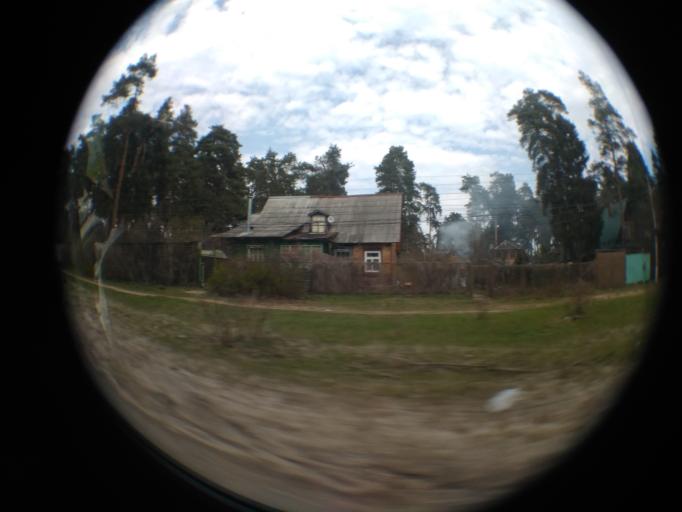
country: RU
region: Moskovskaya
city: Zhukovskiy
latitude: 55.5916
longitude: 38.1479
